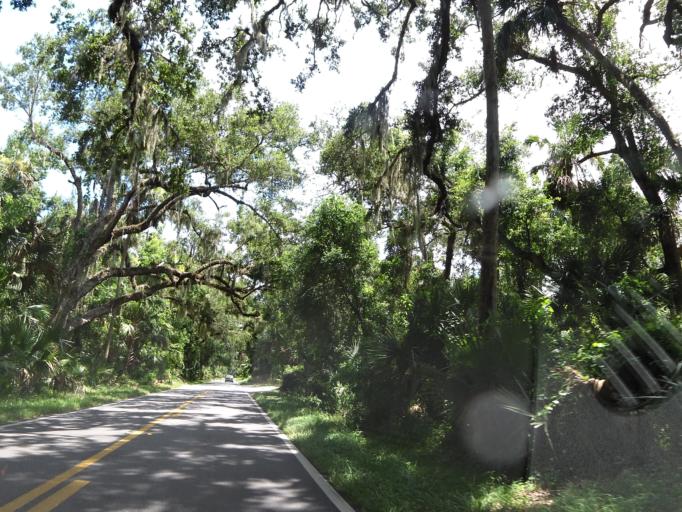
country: US
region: Florida
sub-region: Flagler County
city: Flagler Beach
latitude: 29.4012
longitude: -81.1368
